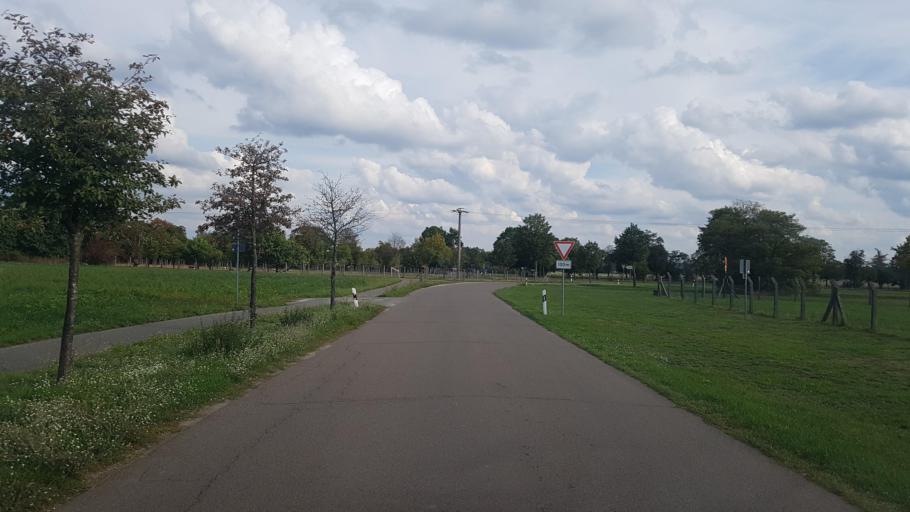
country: DE
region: Brandenburg
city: Dahme
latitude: 51.8578
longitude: 13.4126
